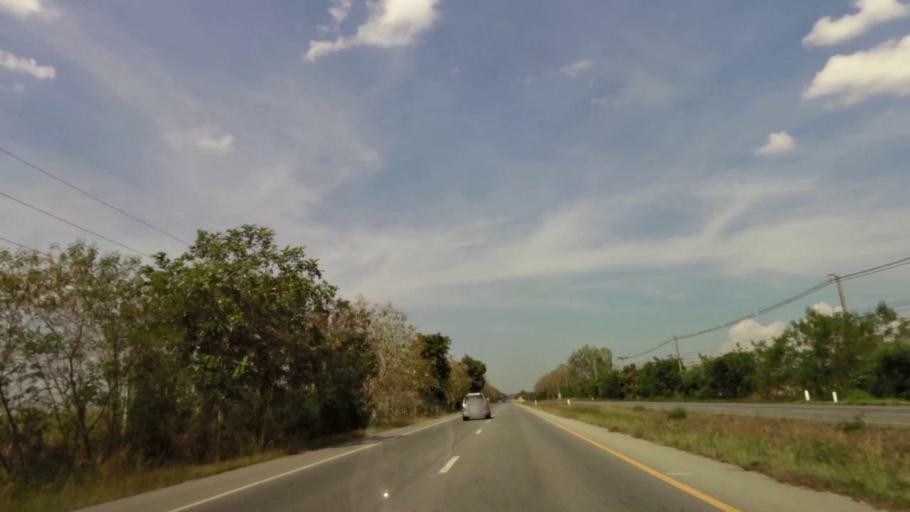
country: TH
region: Uttaradit
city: Tron
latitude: 17.5139
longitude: 100.2225
